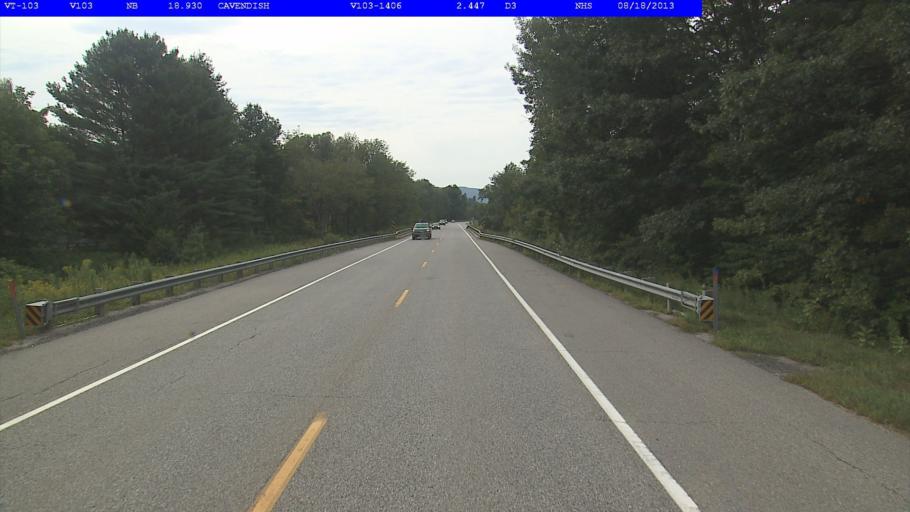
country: US
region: Vermont
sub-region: Windsor County
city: Chester
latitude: 43.3792
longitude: -72.6410
